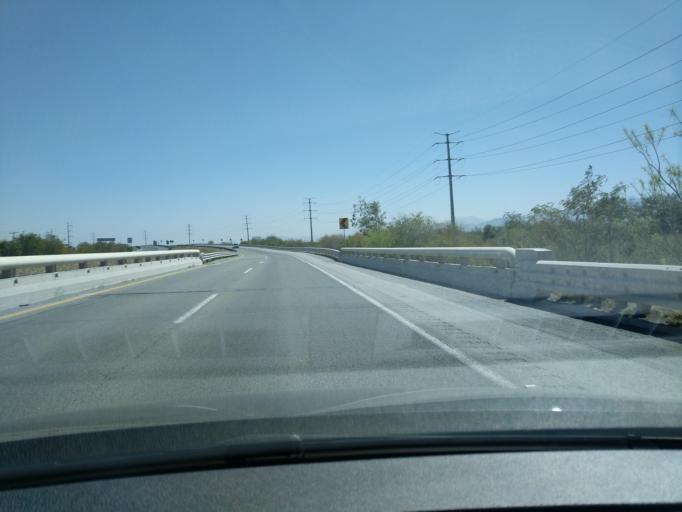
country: MX
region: Nuevo Leon
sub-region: Pesqueria
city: Paseo de San Javier
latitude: 25.7360
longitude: -100.1322
